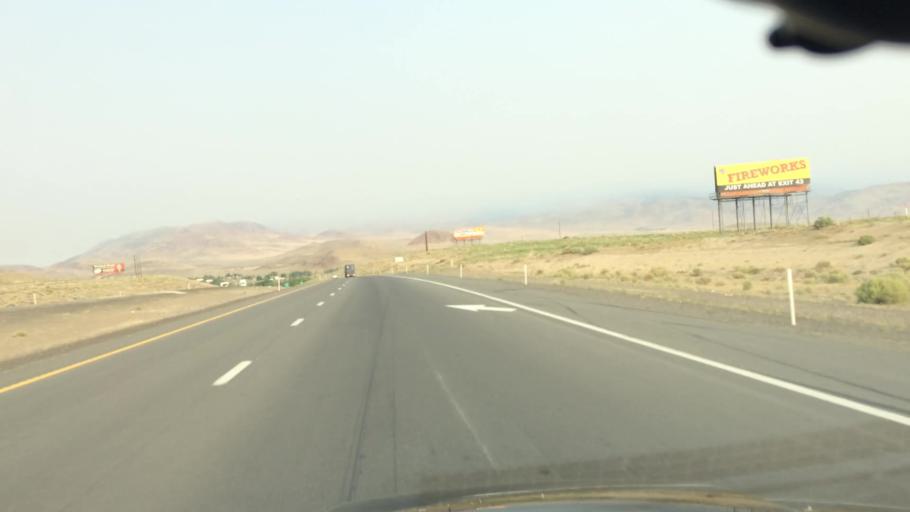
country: US
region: Nevada
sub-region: Lyon County
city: Fernley
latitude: 39.6180
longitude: -119.2775
